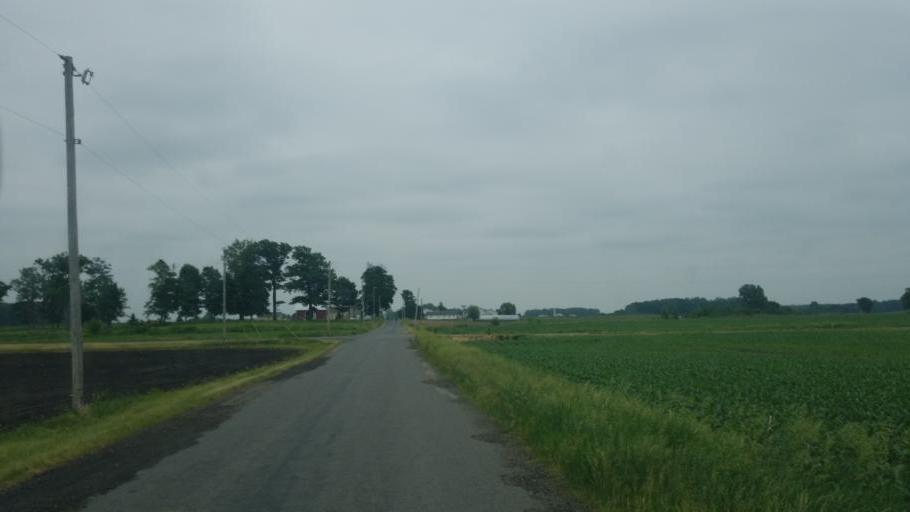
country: US
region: Indiana
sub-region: Marshall County
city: Bremen
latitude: 41.4935
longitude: -86.0993
